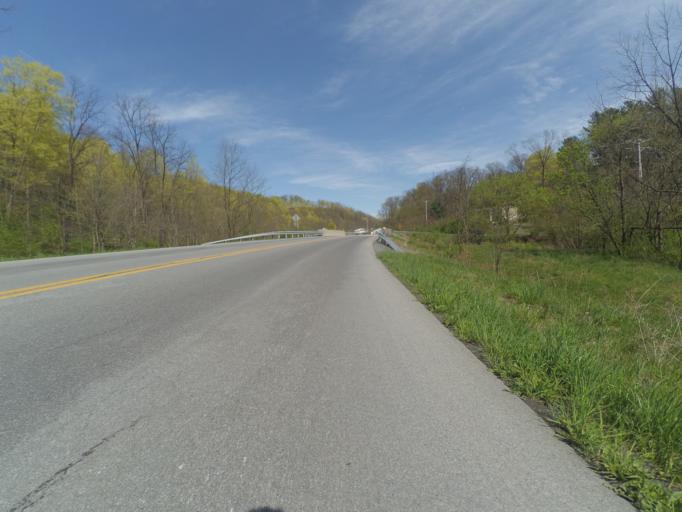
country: US
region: Pennsylvania
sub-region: Blair County
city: Tyrone
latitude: 40.6115
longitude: -78.1881
